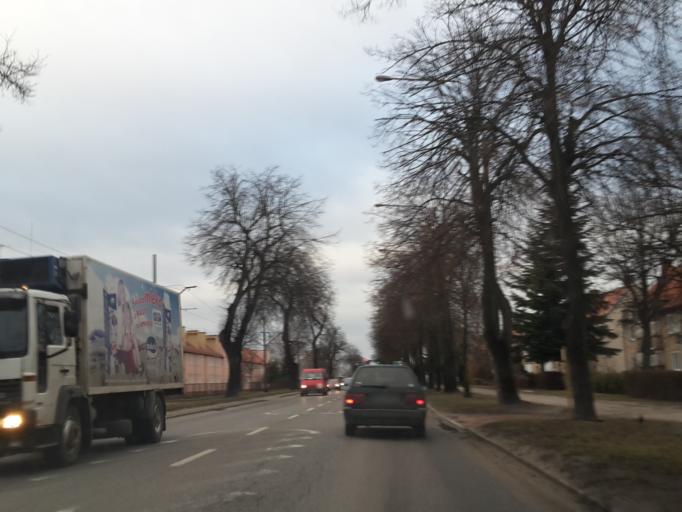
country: PL
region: Warmian-Masurian Voivodeship
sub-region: Powiat elblaski
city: Gronowo Gorne
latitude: 54.1458
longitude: 19.4375
